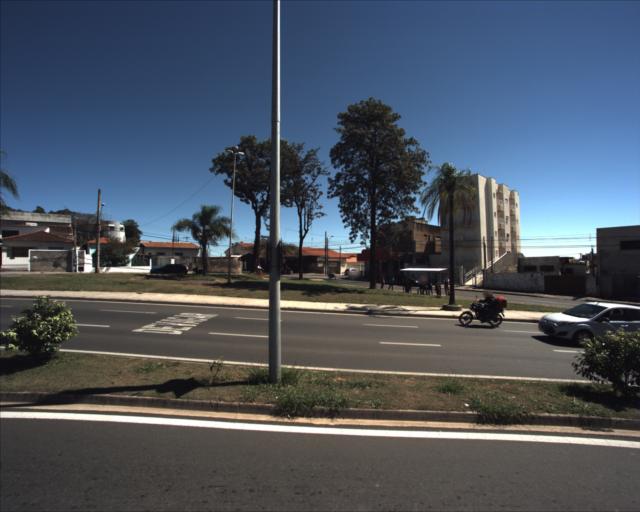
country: BR
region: Sao Paulo
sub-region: Sorocaba
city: Sorocaba
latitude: -23.4986
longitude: -47.4823
